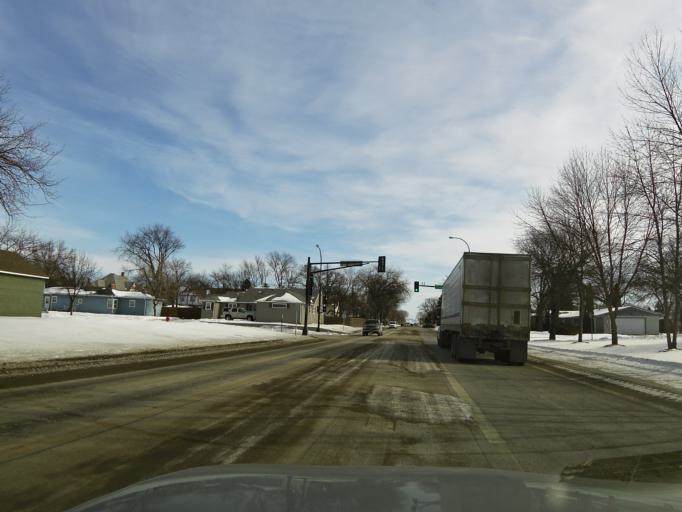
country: US
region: North Dakota
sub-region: Walsh County
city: Grafton
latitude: 48.4125
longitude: -97.4180
